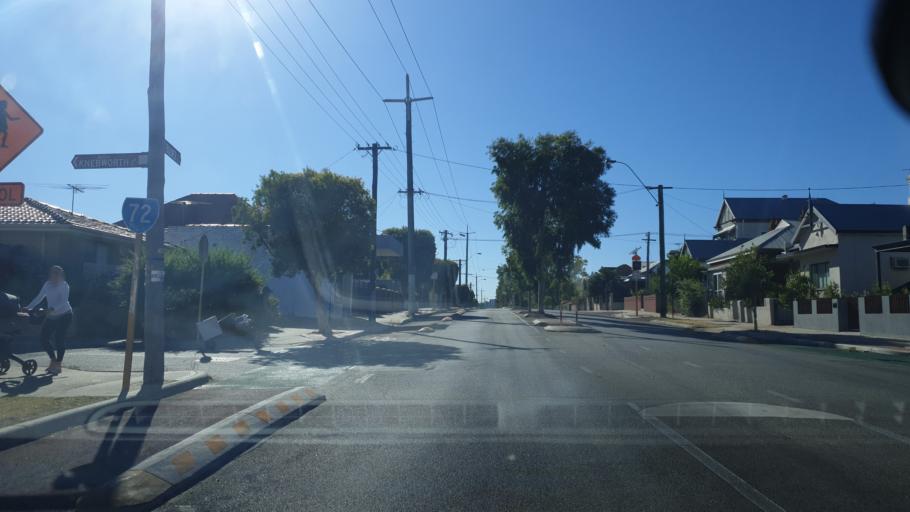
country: AU
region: Western Australia
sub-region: Vincent
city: Mount Lawley
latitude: -31.9413
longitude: 115.8642
